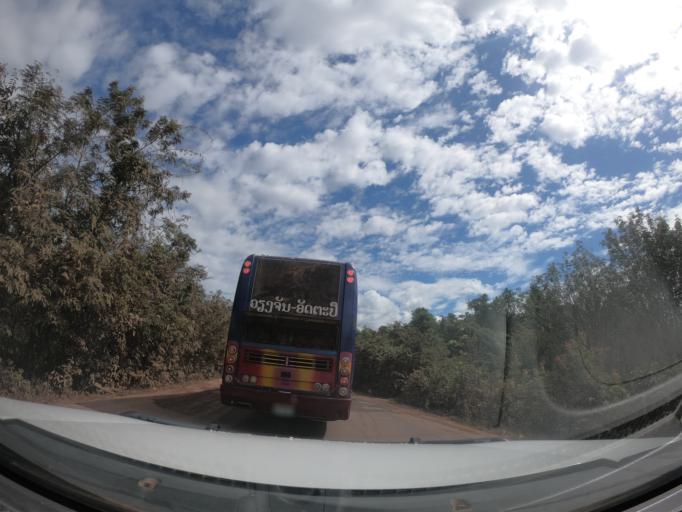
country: LA
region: Bolikhamxai
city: Muang Pakxan
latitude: 18.4407
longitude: 103.5247
